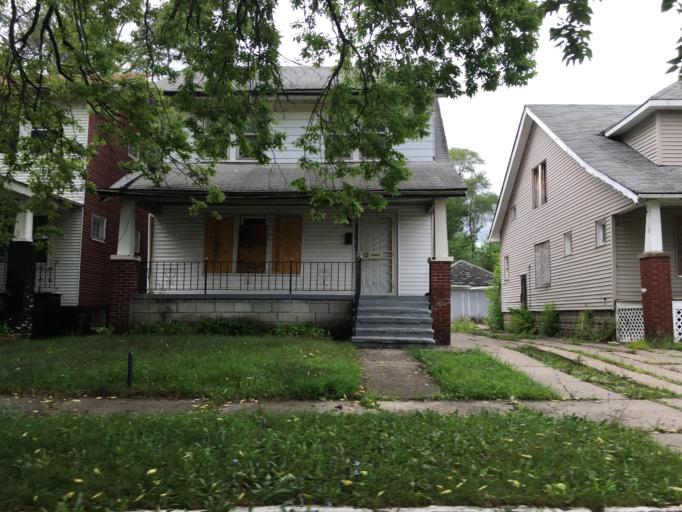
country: US
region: Michigan
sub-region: Wayne County
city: Highland Park
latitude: 42.4092
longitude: -83.1449
